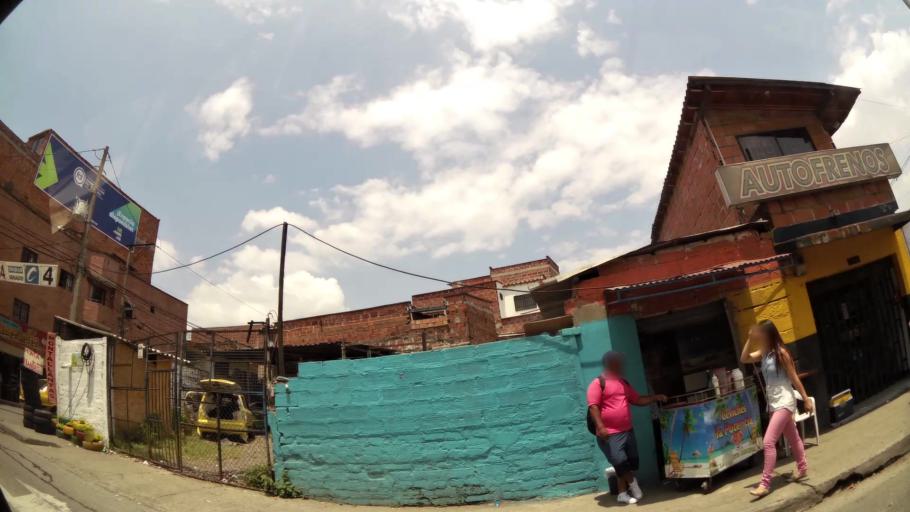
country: CO
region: Antioquia
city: Sabaneta
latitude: 6.1695
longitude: -75.6174
